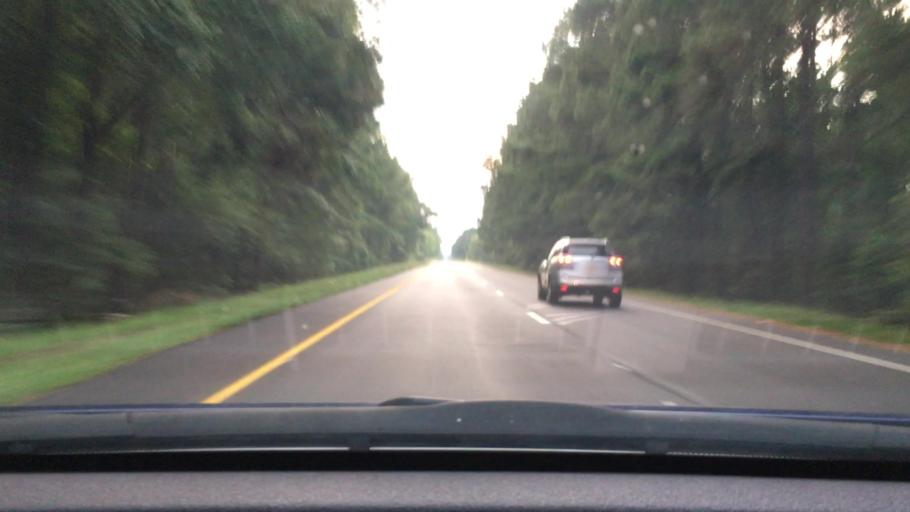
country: US
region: South Carolina
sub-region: Sumter County
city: Stateburg
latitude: 33.9532
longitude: -80.5725
